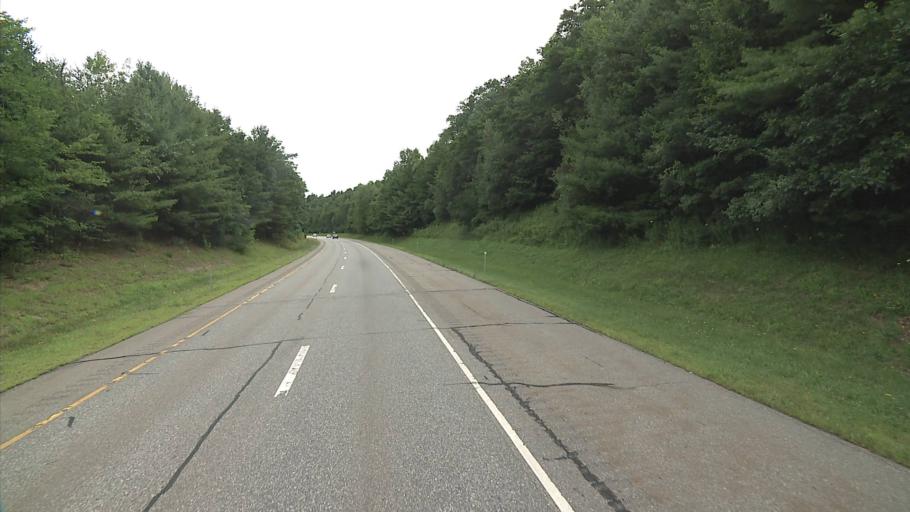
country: US
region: Connecticut
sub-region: Litchfield County
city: Winchester Center
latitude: 41.8575
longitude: -73.0853
